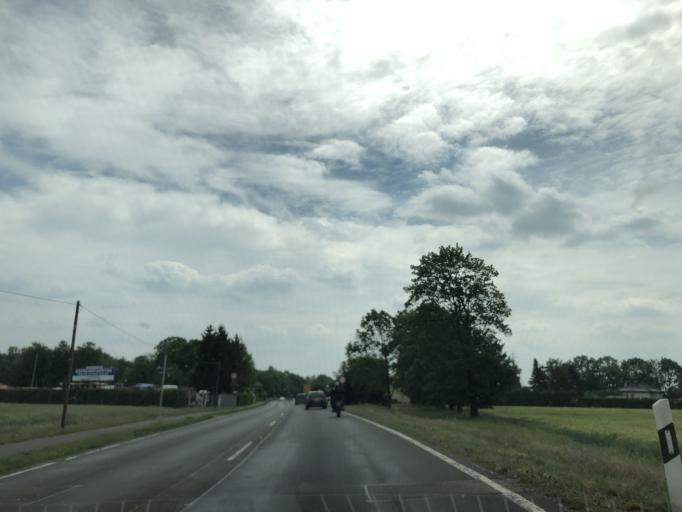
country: DE
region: Brandenburg
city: Wusterhausen
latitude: 52.8997
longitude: 12.4499
